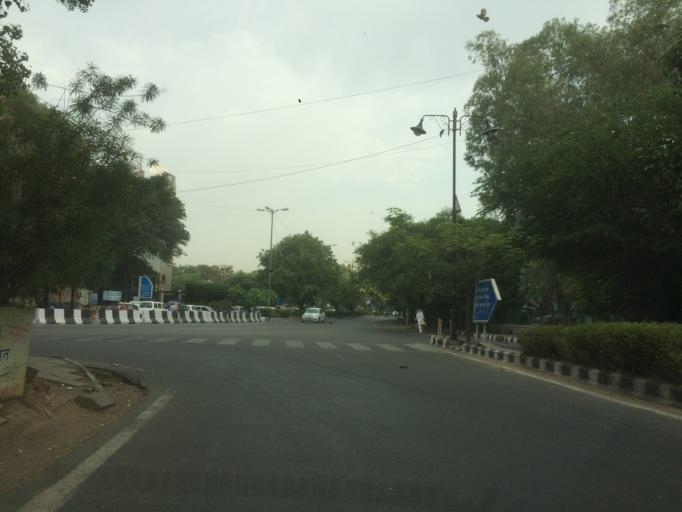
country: IN
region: NCT
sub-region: Central Delhi
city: Karol Bagh
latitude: 28.5727
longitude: 77.1743
